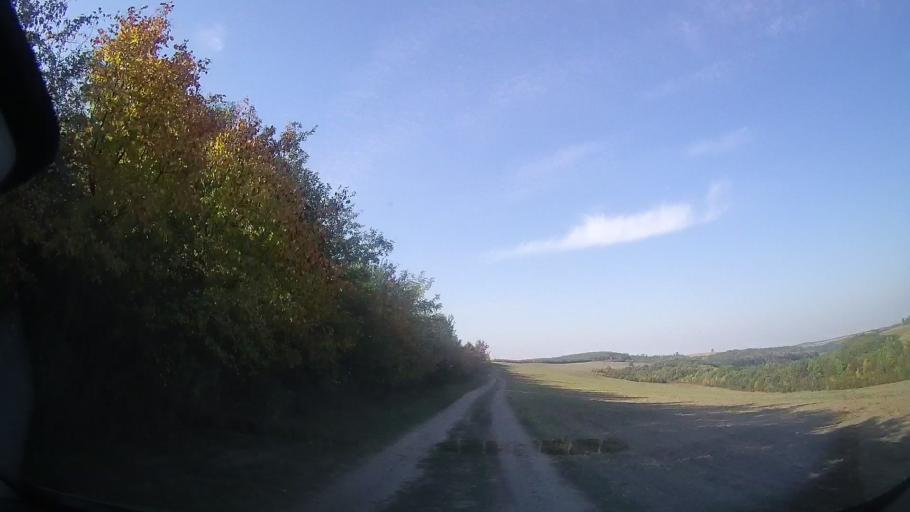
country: RO
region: Timis
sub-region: Comuna Bogda
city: Bogda
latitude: 45.9143
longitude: 21.6083
